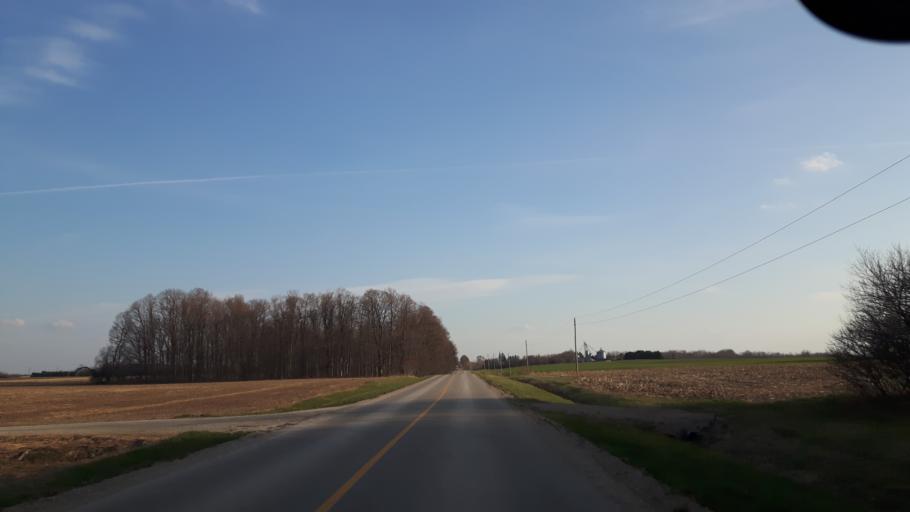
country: CA
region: Ontario
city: Goderich
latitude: 43.6524
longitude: -81.6643
